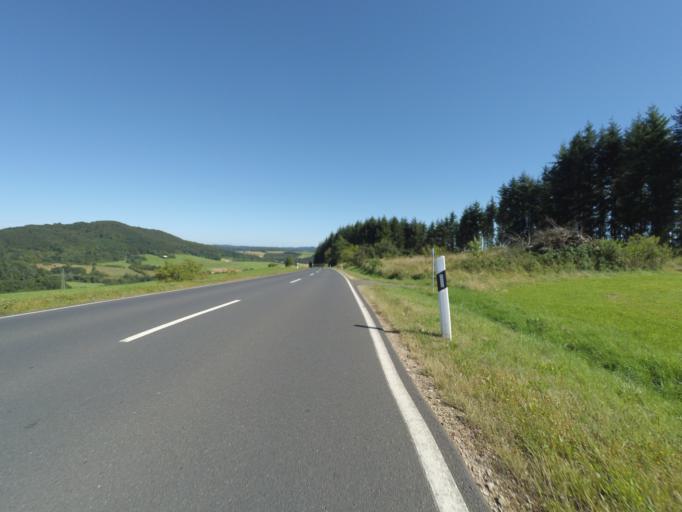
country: DE
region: Rheinland-Pfalz
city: Hinterweiler
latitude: 50.2145
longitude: 6.7791
